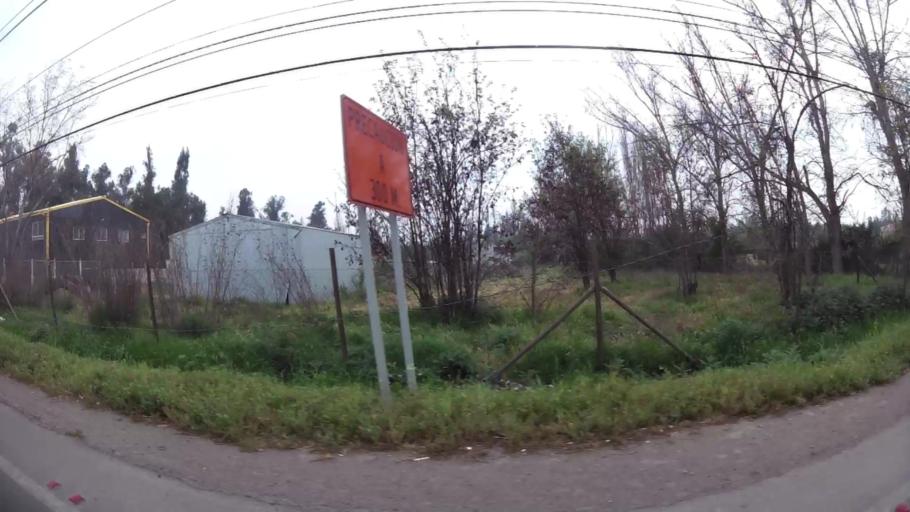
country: CL
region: Santiago Metropolitan
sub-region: Provincia de Chacabuco
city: Lampa
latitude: -33.2307
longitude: -70.7888
